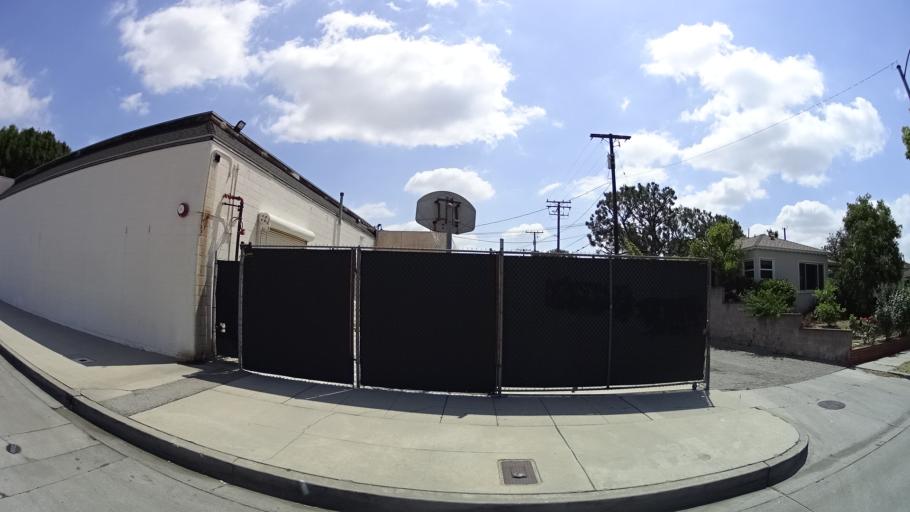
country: US
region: California
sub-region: Los Angeles County
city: North Hollywood
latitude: 34.1644
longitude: -118.3572
